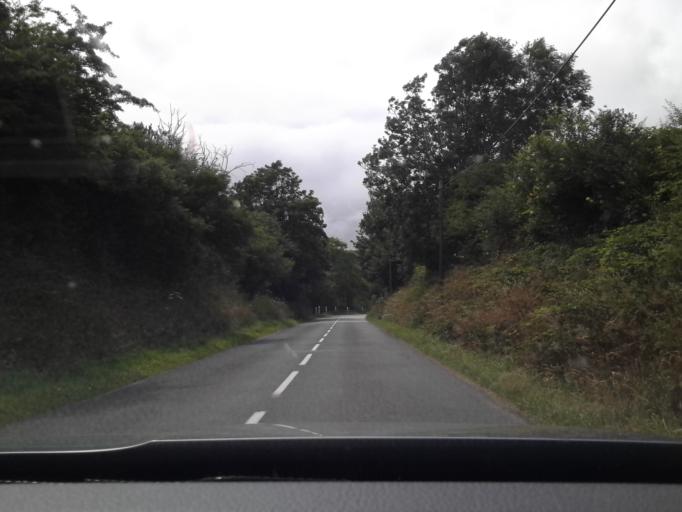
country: FR
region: Lower Normandy
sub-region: Departement de la Manche
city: Urville-Nacqueville
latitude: 49.6736
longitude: -1.7878
